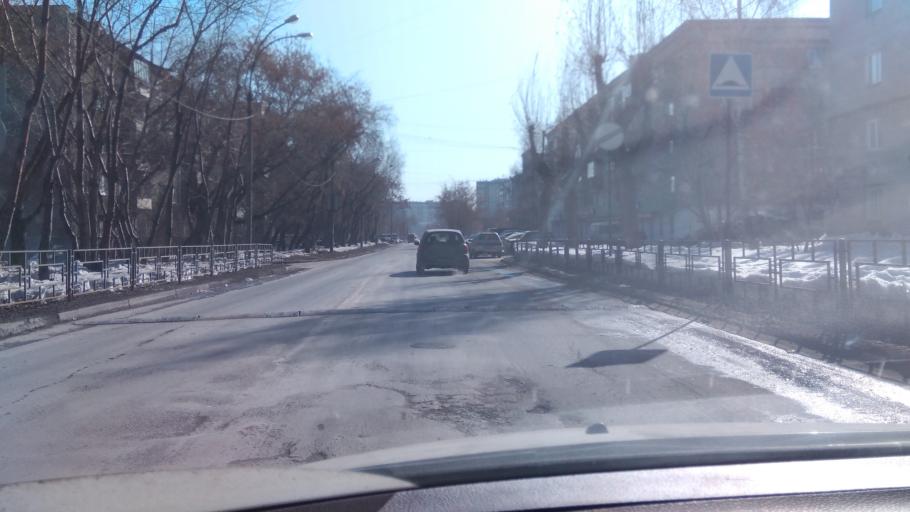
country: RU
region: Sverdlovsk
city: Shuvakish
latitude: 56.8694
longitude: 60.5322
